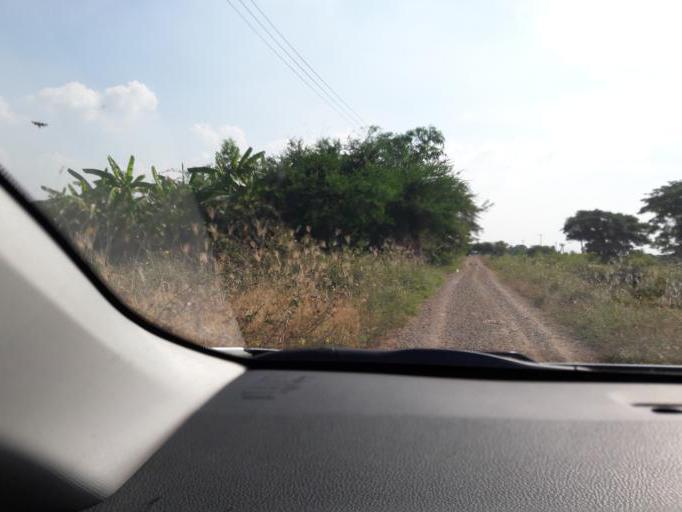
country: TH
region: Ang Thong
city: Wiset Chaichan
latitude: 14.5584
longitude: 100.3896
